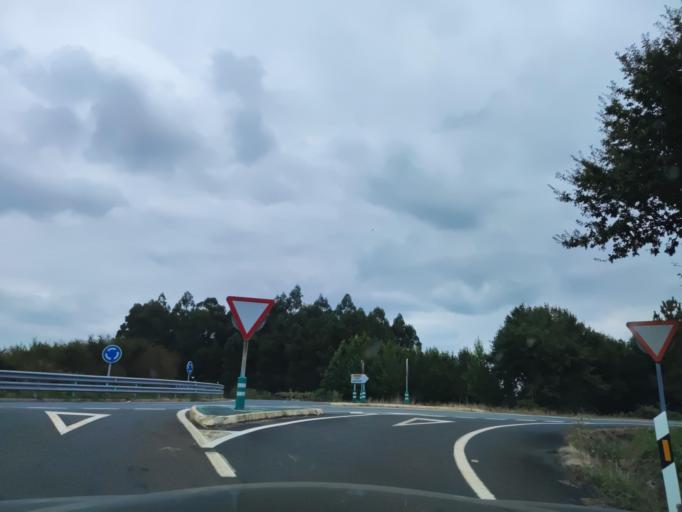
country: ES
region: Galicia
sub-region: Provincia da Coruna
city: Teo
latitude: 42.7987
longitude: -8.5353
